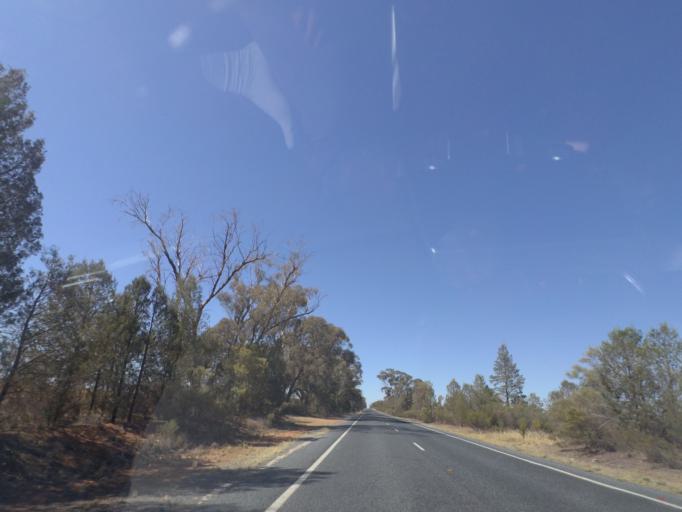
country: AU
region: New South Wales
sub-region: Bland
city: West Wyalong
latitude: -34.1525
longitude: 147.1182
